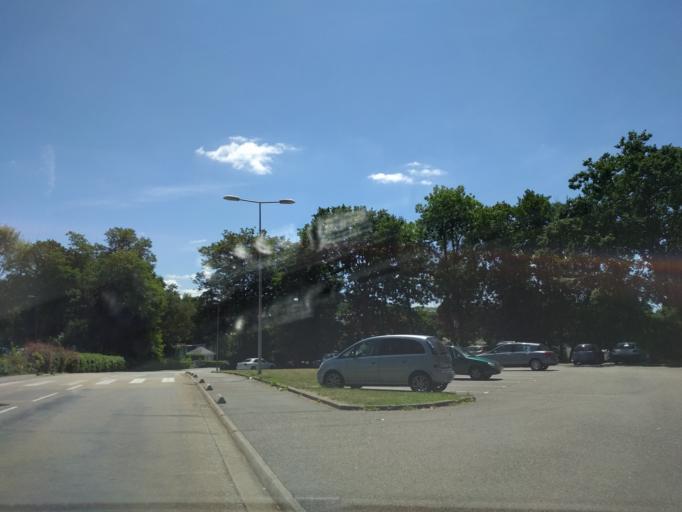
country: FR
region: Brittany
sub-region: Departement du Finistere
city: Quimper
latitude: 47.9774
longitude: -4.0974
